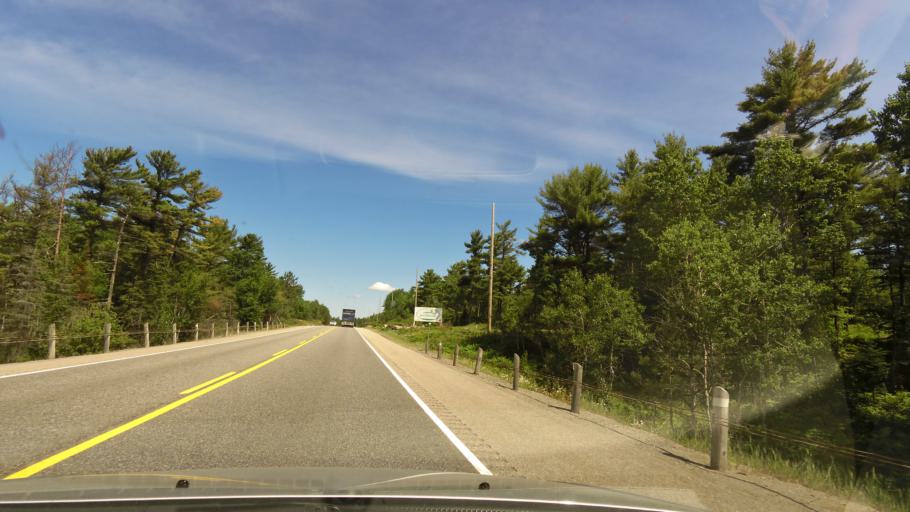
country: CA
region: Ontario
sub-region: Parry Sound District
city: Parry Sound
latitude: 45.6389
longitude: -80.3974
